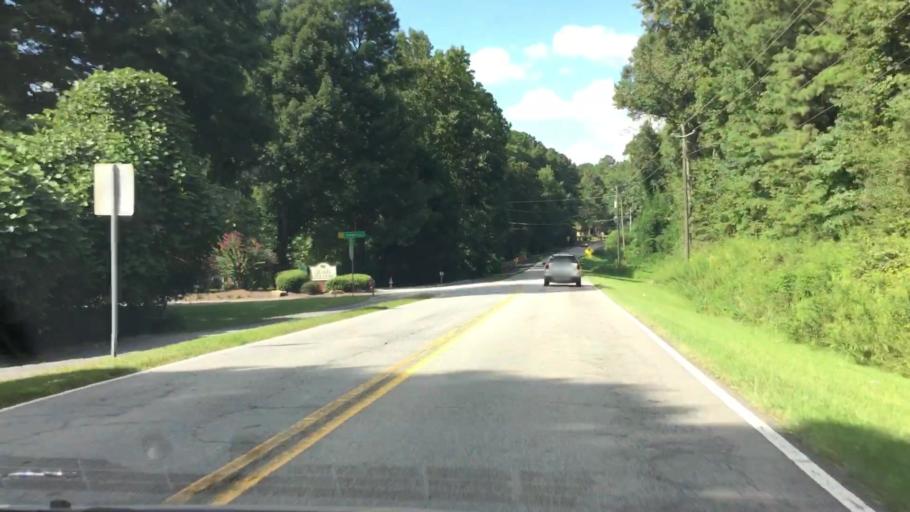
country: US
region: Georgia
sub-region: Fayette County
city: Fayetteville
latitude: 33.4332
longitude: -84.4601
